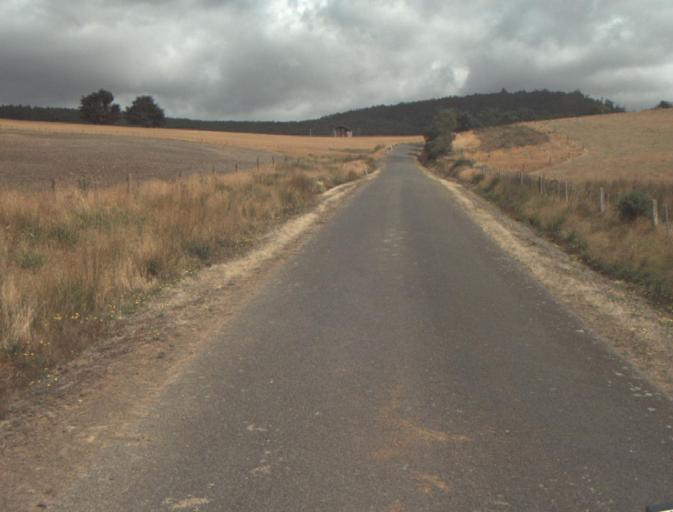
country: AU
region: Tasmania
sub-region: Northern Midlands
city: Evandale
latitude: -41.4777
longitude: 147.4993
